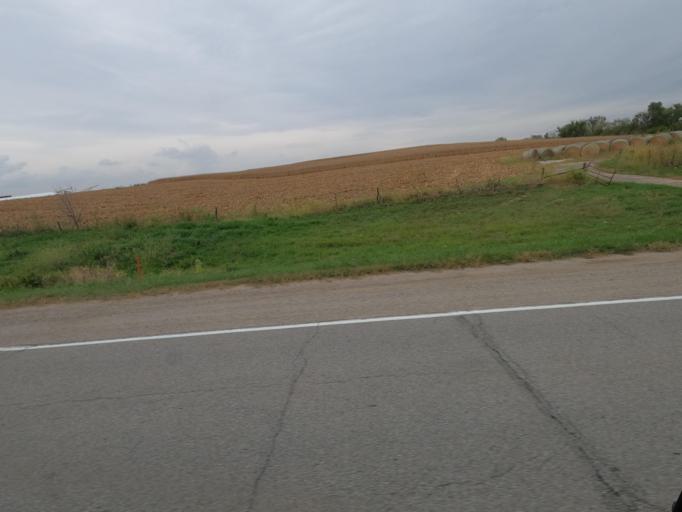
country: US
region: Iowa
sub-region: Van Buren County
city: Keosauqua
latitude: 40.8568
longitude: -92.0856
